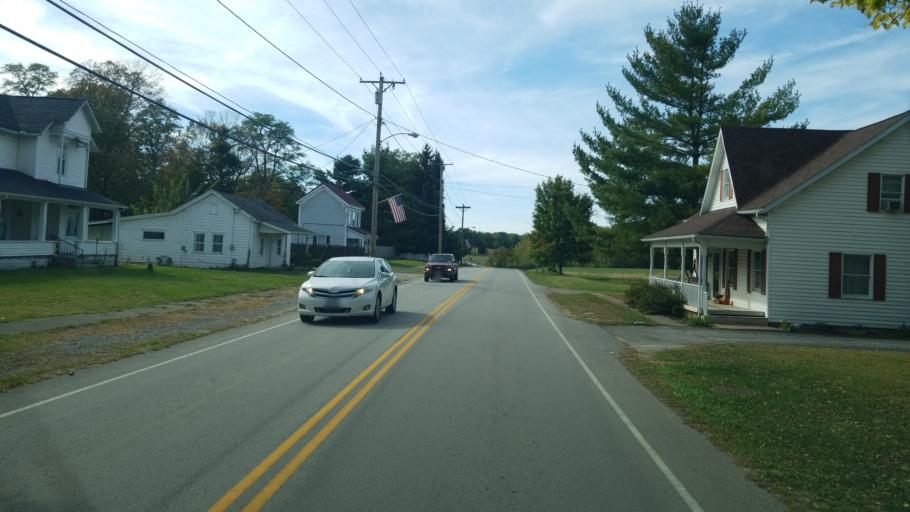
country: US
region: Ohio
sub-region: Highland County
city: Leesburg
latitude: 39.3439
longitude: -83.6013
